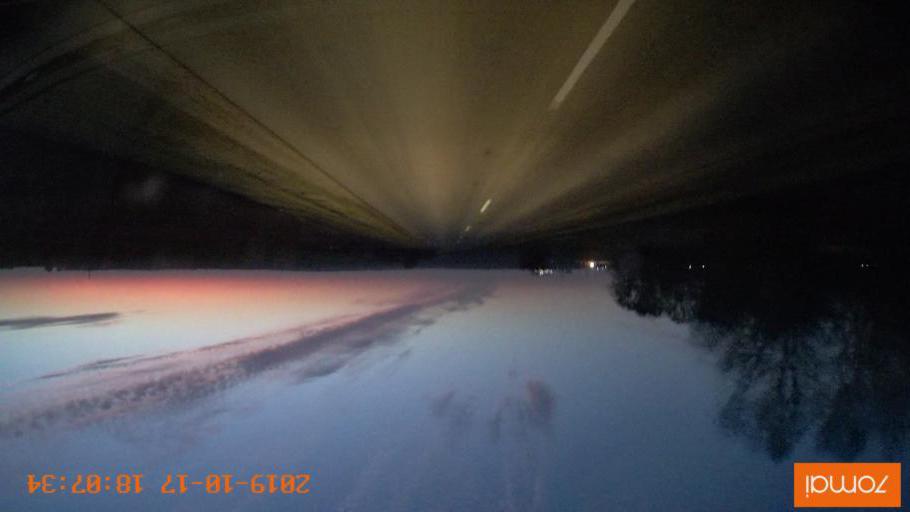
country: RU
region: Tula
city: Kurkino
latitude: 53.4428
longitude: 38.6532
